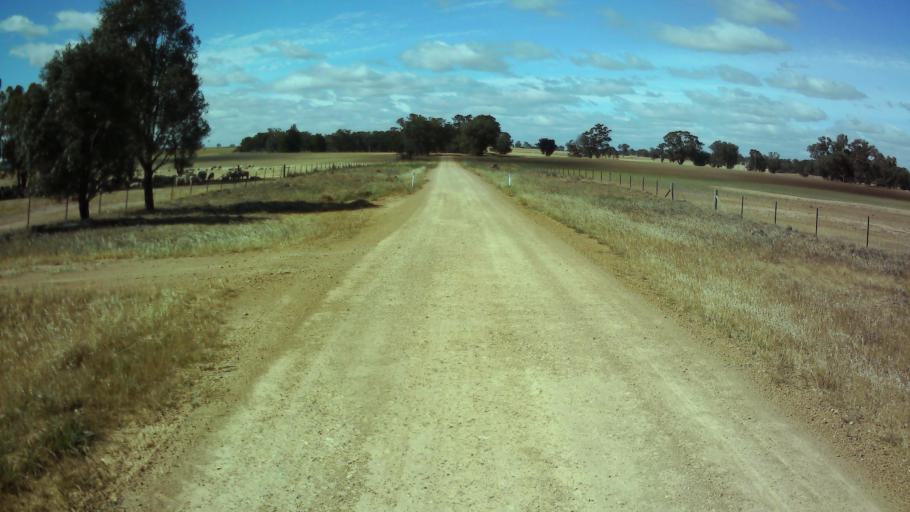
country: AU
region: New South Wales
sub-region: Weddin
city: Grenfell
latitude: -34.0607
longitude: 148.3121
